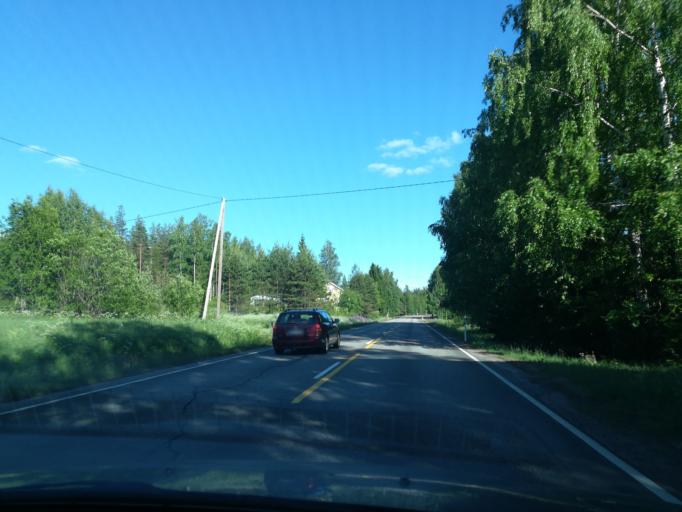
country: FI
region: South Karelia
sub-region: Imatra
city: Ruokolahti
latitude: 61.3722
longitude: 28.6681
